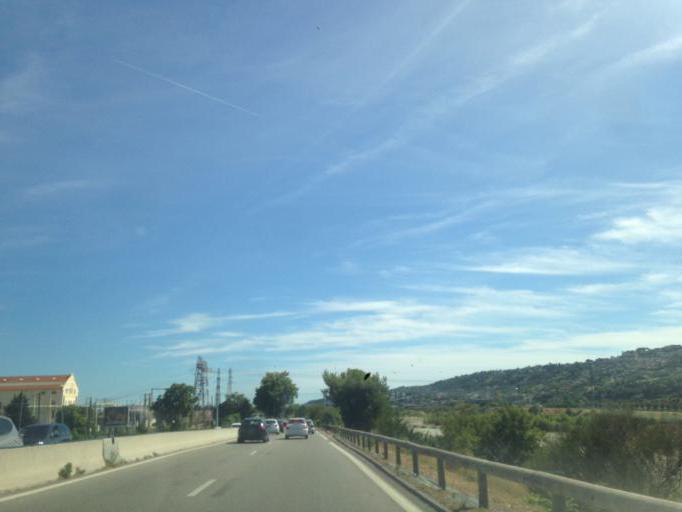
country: FR
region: Provence-Alpes-Cote d'Azur
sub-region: Departement des Alpes-Maritimes
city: La Gaude
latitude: 43.7219
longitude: 7.1862
